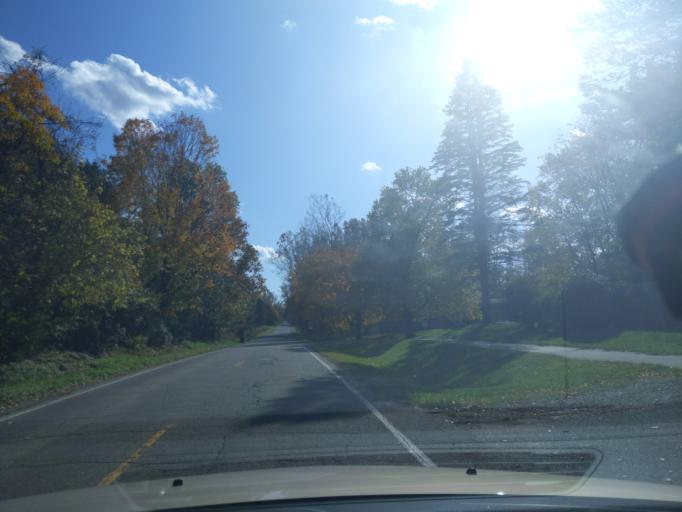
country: US
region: Michigan
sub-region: Ingham County
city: Haslett
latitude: 42.7424
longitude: -84.3931
